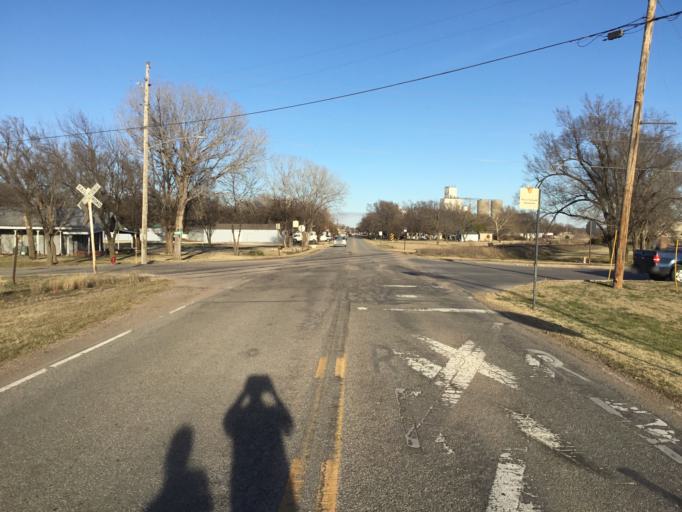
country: US
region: Kansas
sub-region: Sedgwick County
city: Valley Center
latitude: 37.8322
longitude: -97.3815
